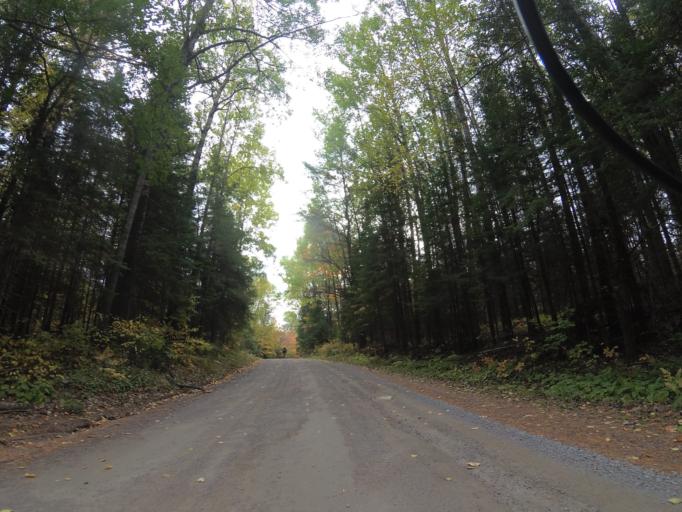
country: CA
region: Ontario
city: Pembroke
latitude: 45.2597
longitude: -77.2097
